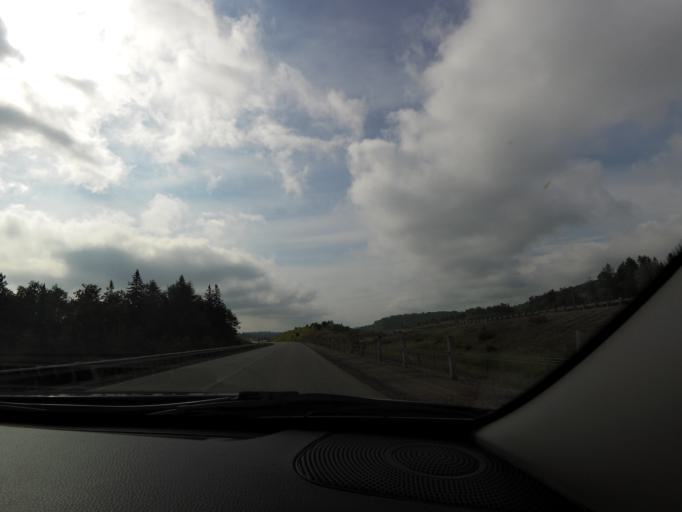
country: CA
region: Ontario
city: Huntsville
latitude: 45.5159
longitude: -79.3095
